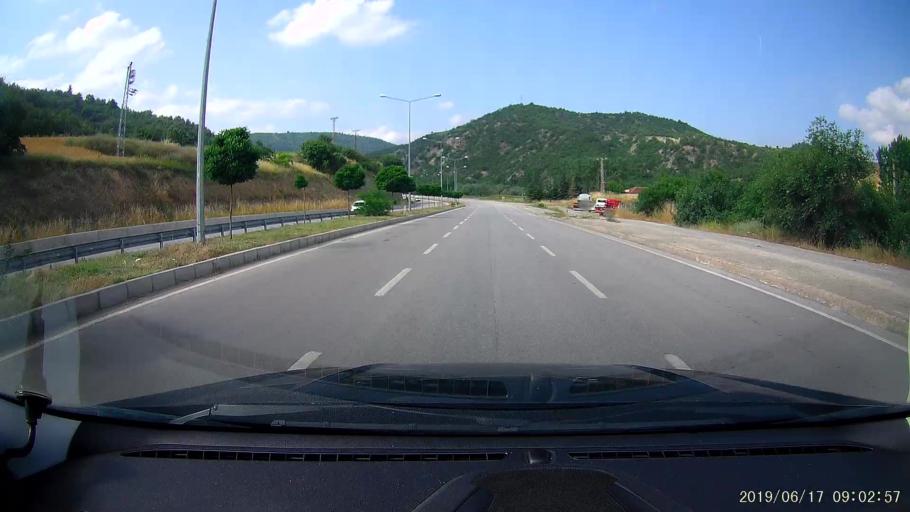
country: TR
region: Amasya
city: Tasova
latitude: 40.7610
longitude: 36.3039
